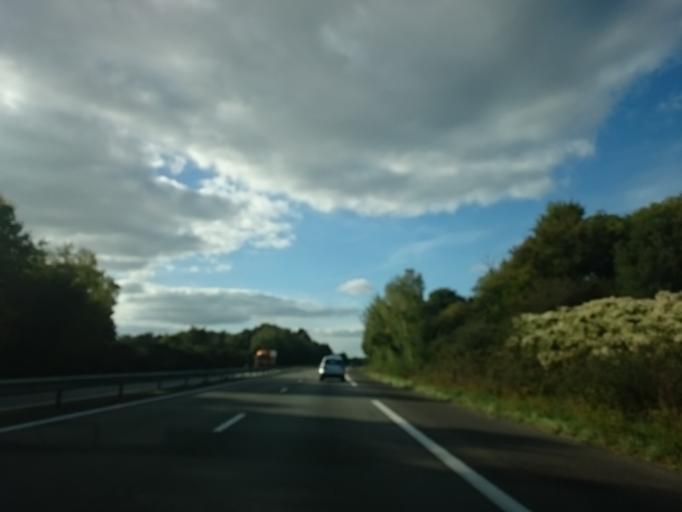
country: FR
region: Pays de la Loire
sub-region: Departement de la Loire-Atlantique
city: Treillieres
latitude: 47.3022
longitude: -1.6305
